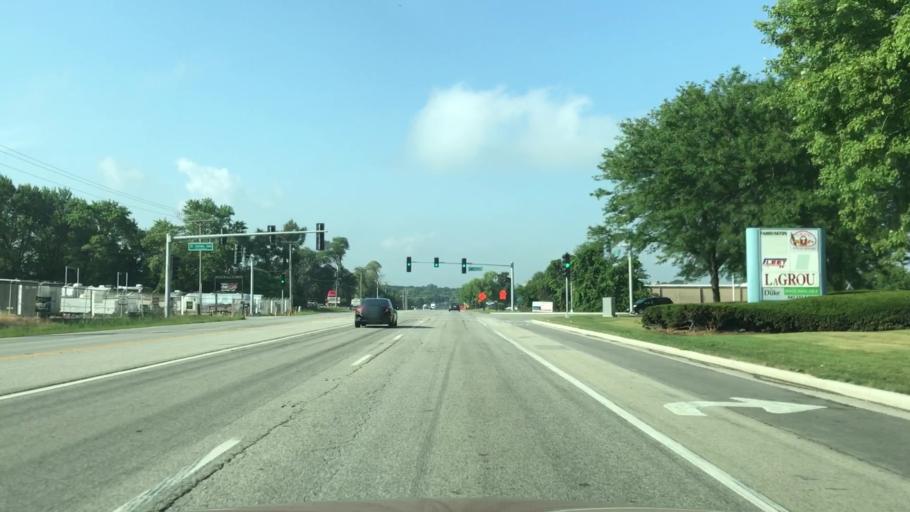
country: US
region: Illinois
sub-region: Will County
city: Bolingbrook
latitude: 41.6808
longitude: -88.0530
